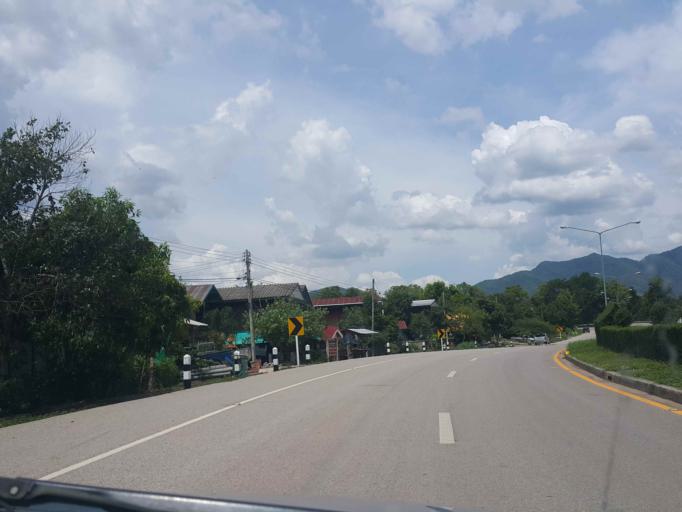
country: TH
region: Nan
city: Ban Luang
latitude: 18.8497
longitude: 100.4276
